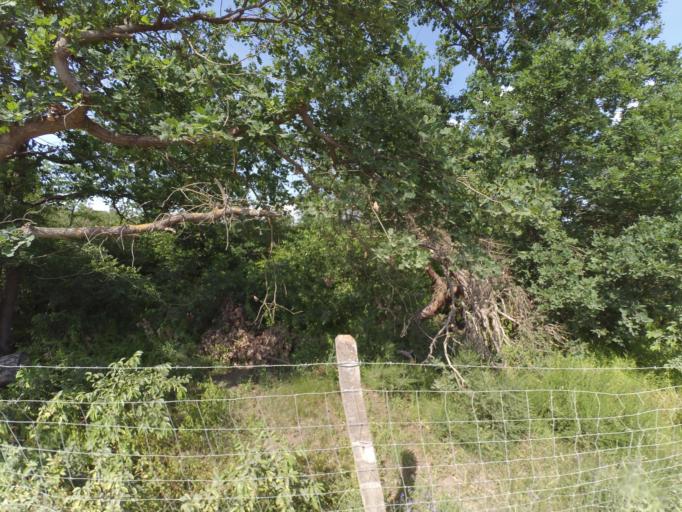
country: DE
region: Hesse
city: Lampertheim
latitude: 49.6211
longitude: 8.4832
